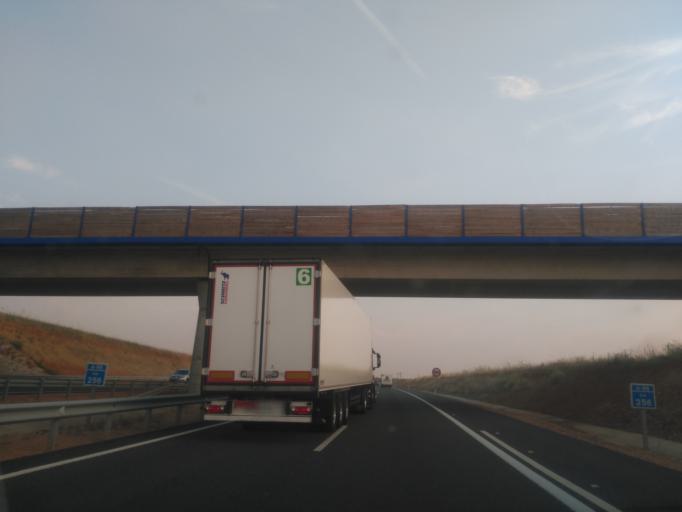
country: ES
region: Castille and Leon
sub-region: Provincia de Zamora
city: Montamarta
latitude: 41.6824
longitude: -5.8056
